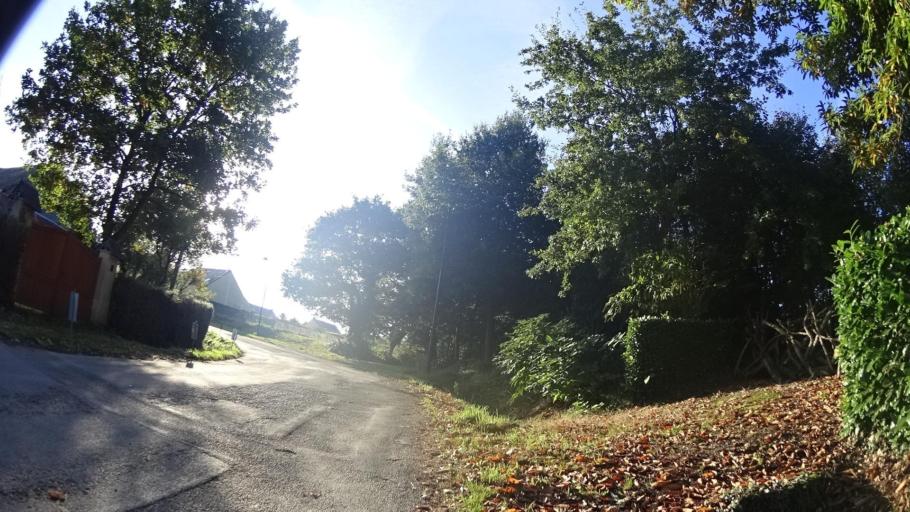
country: FR
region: Brittany
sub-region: Departement des Cotes-d'Armor
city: Evran
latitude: 48.3379
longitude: -1.9371
